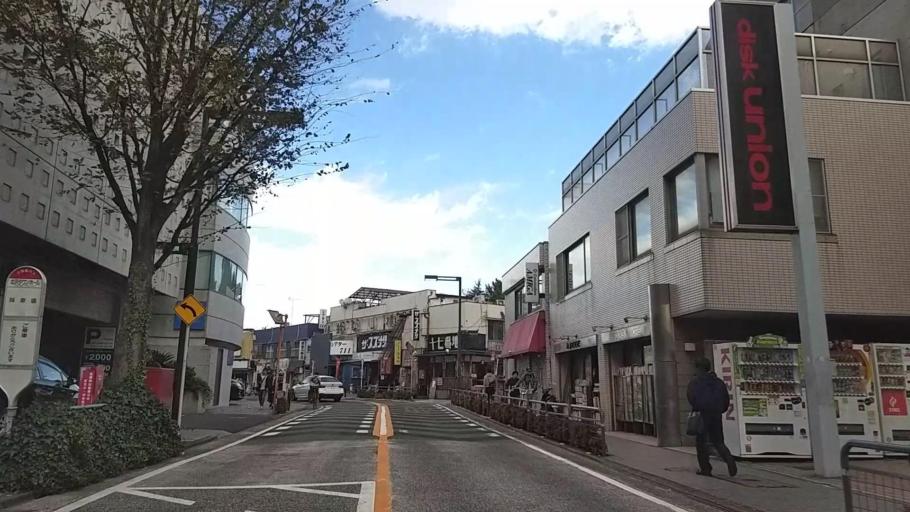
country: JP
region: Tokyo
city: Tokyo
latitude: 35.6621
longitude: 139.6700
